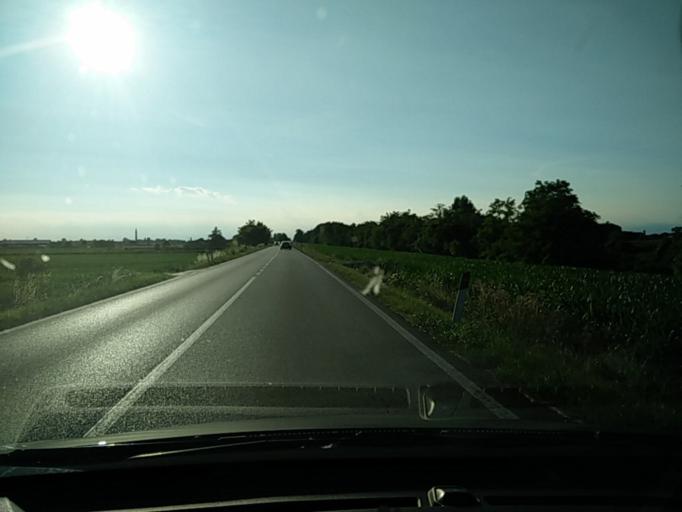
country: IT
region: Veneto
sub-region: Provincia di Venezia
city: Passarella
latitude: 45.5916
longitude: 12.6262
